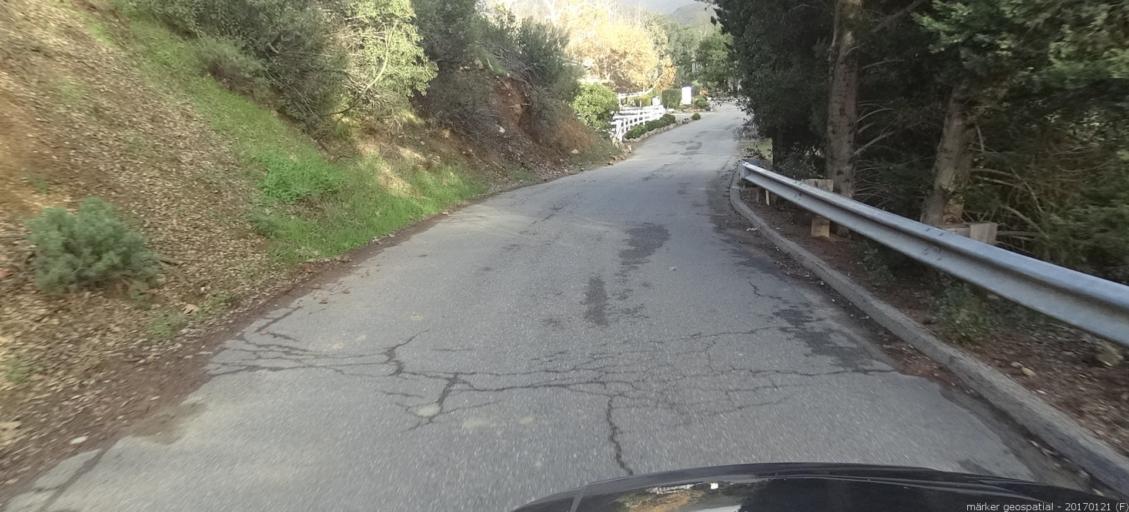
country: US
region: California
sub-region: Orange County
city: Portola Hills
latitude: 33.7089
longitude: -117.6362
